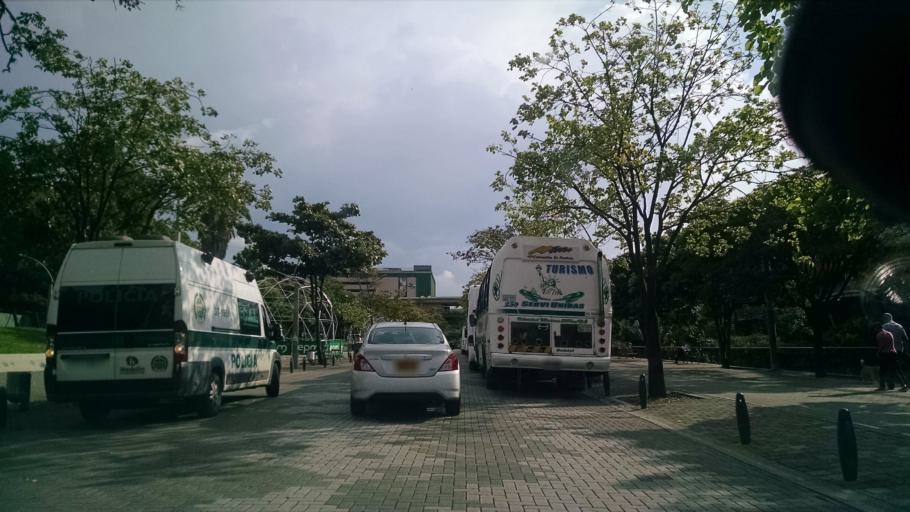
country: CO
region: Antioquia
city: Medellin
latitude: 6.2715
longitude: -75.5652
